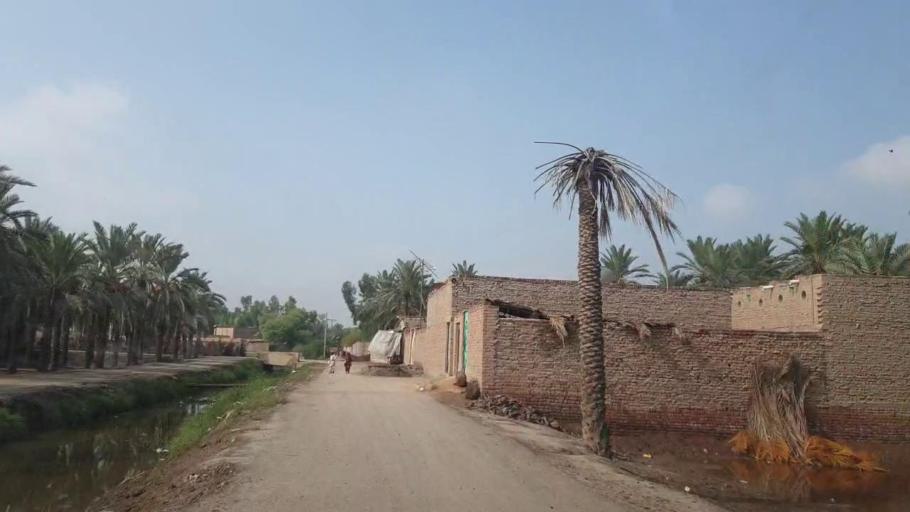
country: PK
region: Sindh
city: Khairpur
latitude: 27.5856
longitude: 68.7745
